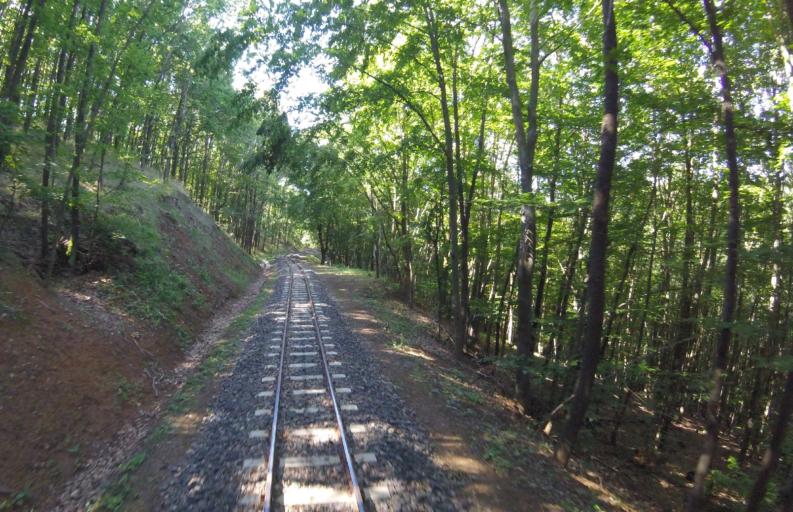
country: HU
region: Pest
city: Szob
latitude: 47.8939
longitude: 18.8782
